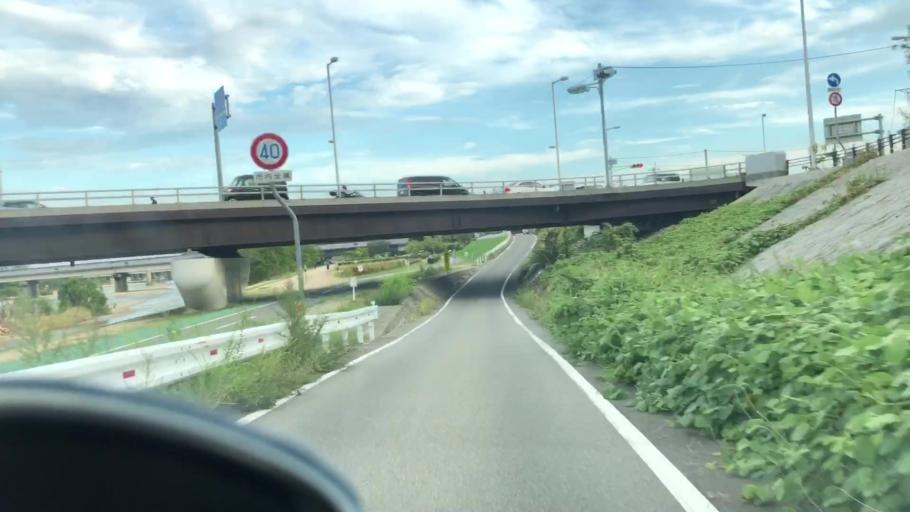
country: JP
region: Hyogo
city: Itami
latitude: 34.7479
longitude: 135.3749
